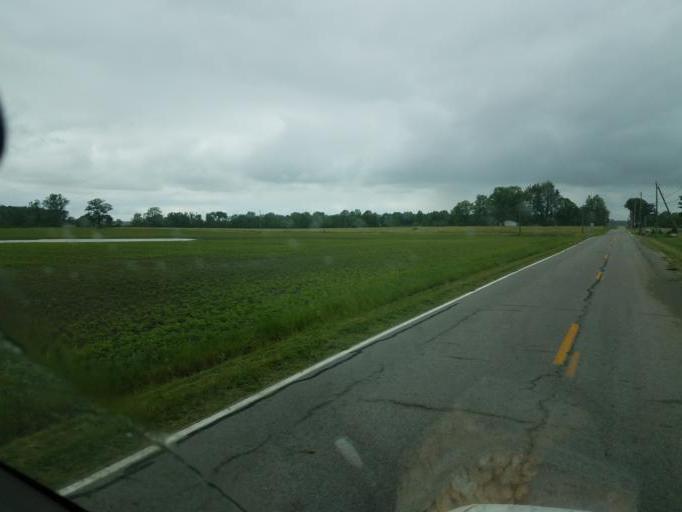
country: US
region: Ohio
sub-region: Marion County
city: Marion
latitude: 40.5641
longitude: -83.0366
